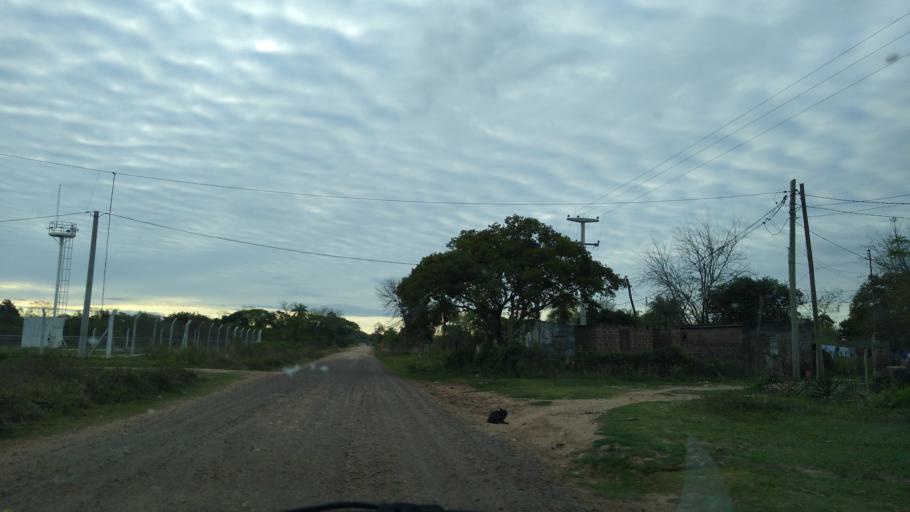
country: AR
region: Chaco
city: Fontana
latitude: -27.3994
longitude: -59.0447
